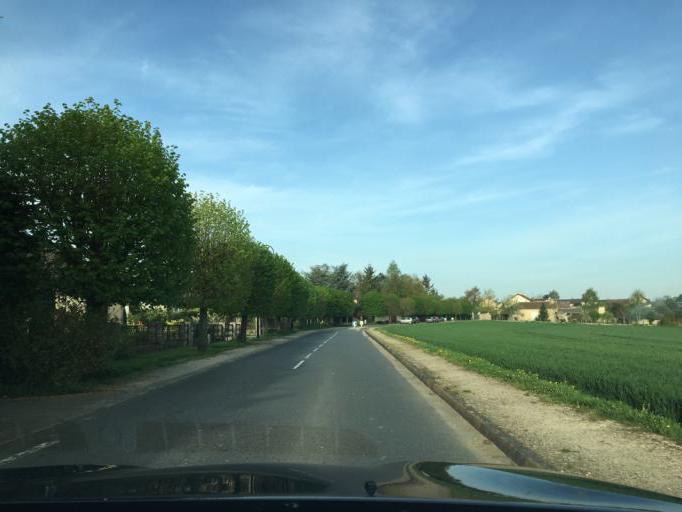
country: FR
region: Ile-de-France
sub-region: Departement des Yvelines
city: Gazeran
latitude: 48.5780
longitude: 1.7866
